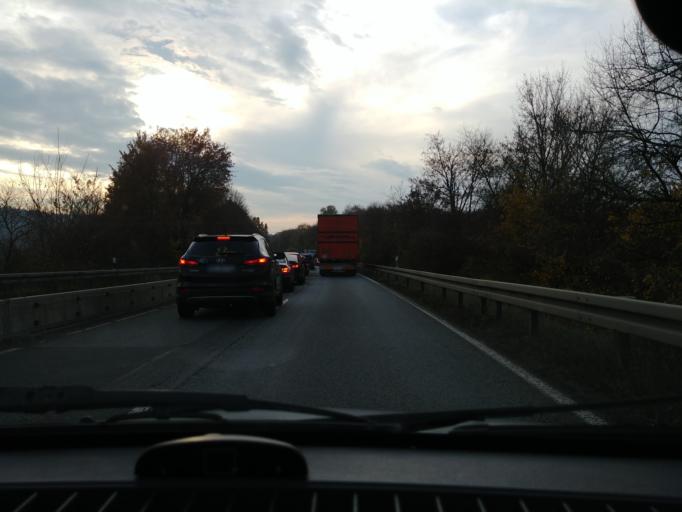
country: DE
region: Hesse
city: Leun
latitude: 50.5377
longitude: 8.3261
